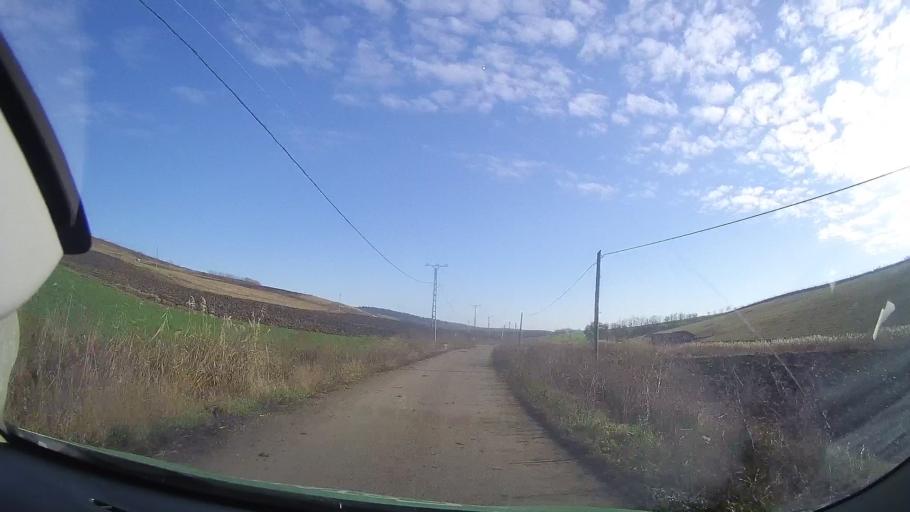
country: RO
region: Mures
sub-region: Comuna Saulia
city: Saulia
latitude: 46.6147
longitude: 24.2417
